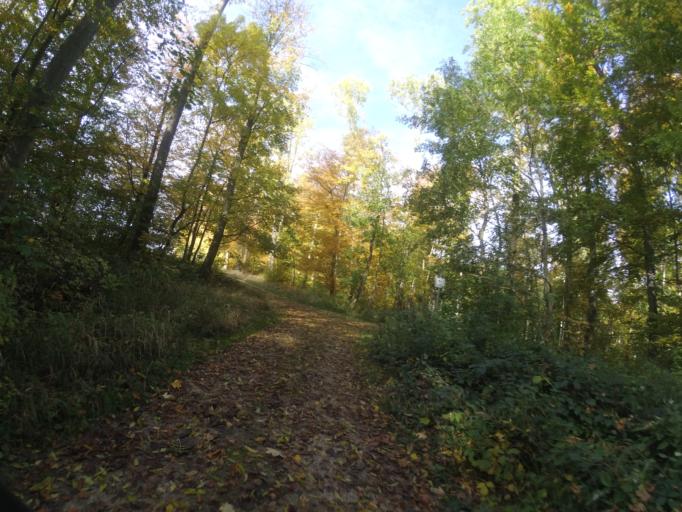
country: DE
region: Baden-Wuerttemberg
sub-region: Tuebingen Region
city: Amstetten
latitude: 48.6100
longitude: 9.9151
